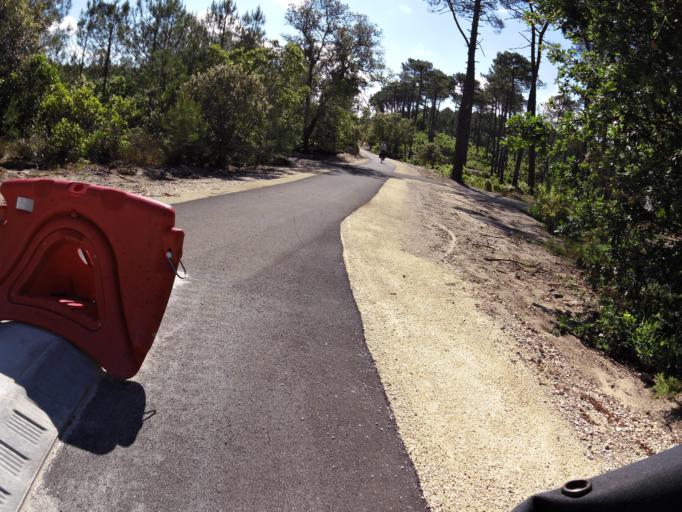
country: FR
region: Aquitaine
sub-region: Departement de la Gironde
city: Lacanau
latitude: 45.0298
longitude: -1.1750
